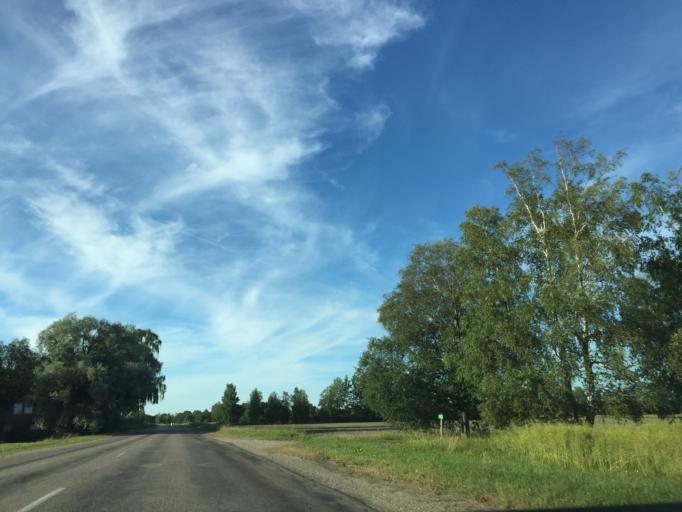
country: LV
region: Ventspils
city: Ventspils
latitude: 57.3191
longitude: 21.5600
